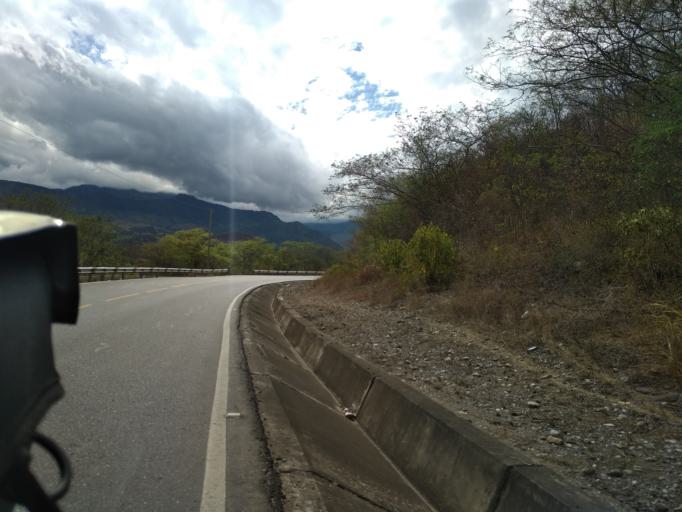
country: PE
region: Amazonas
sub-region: Utcubamba
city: Jamalca
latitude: -5.8245
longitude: -78.2585
